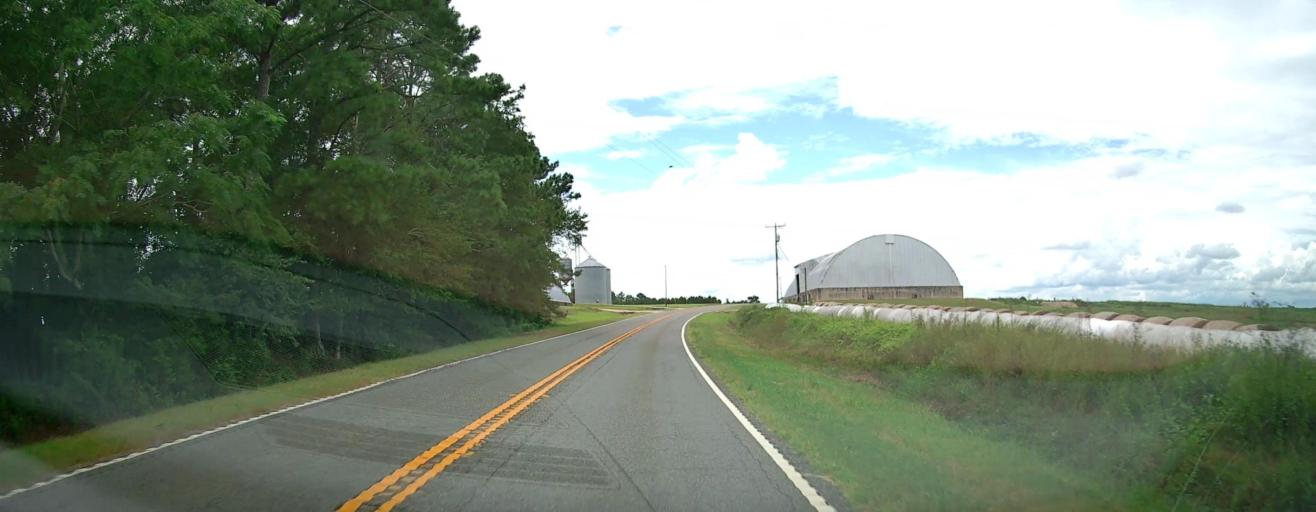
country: US
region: Georgia
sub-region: Dooly County
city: Unadilla
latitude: 32.2594
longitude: -83.8025
